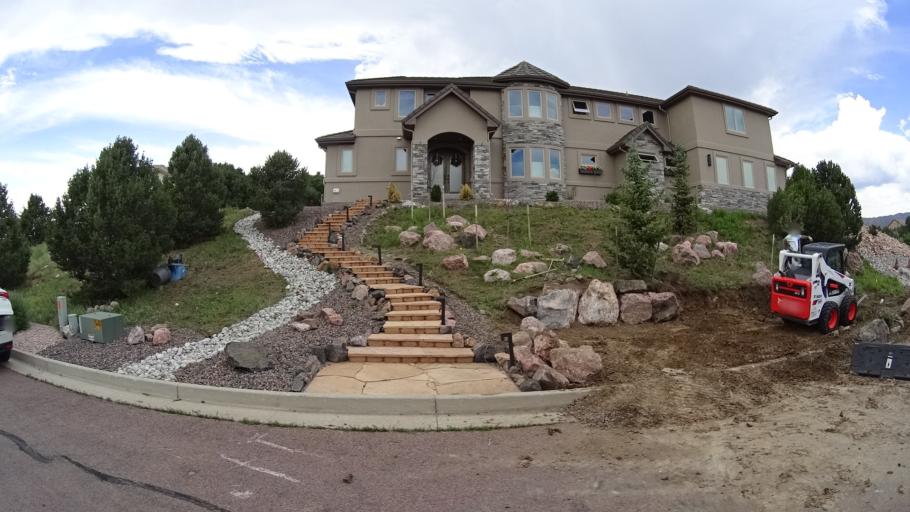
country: US
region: Colorado
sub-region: El Paso County
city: Colorado Springs
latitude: 38.9085
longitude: -104.8326
